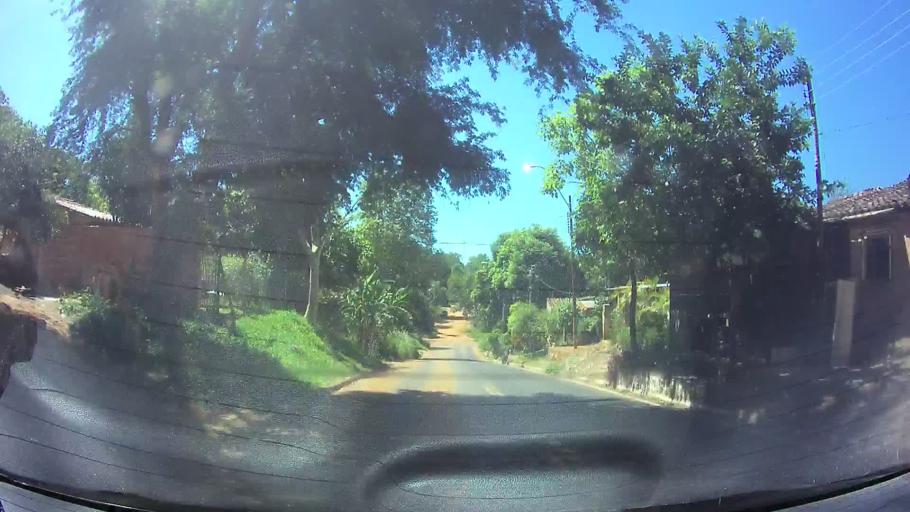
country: PY
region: Central
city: Aregua
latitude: -25.3180
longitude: -57.3903
